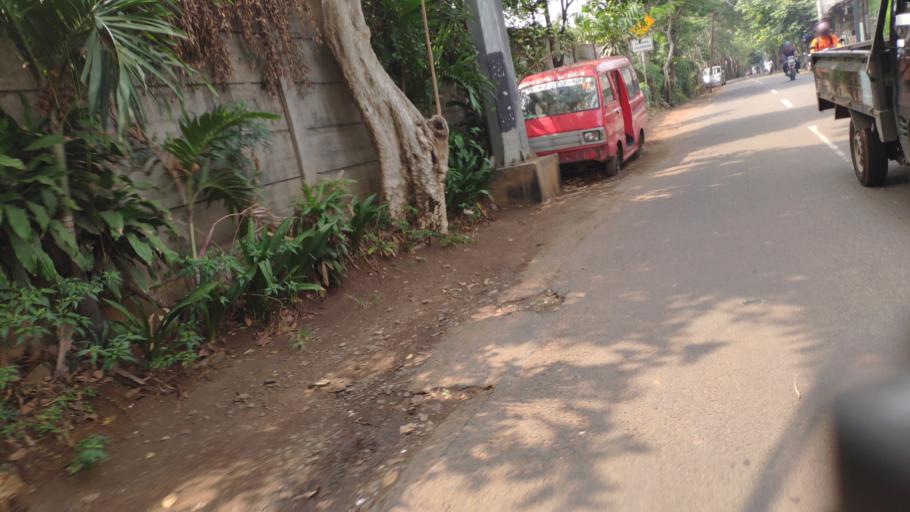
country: ID
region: West Java
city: Depok
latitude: -6.3234
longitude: 106.8228
